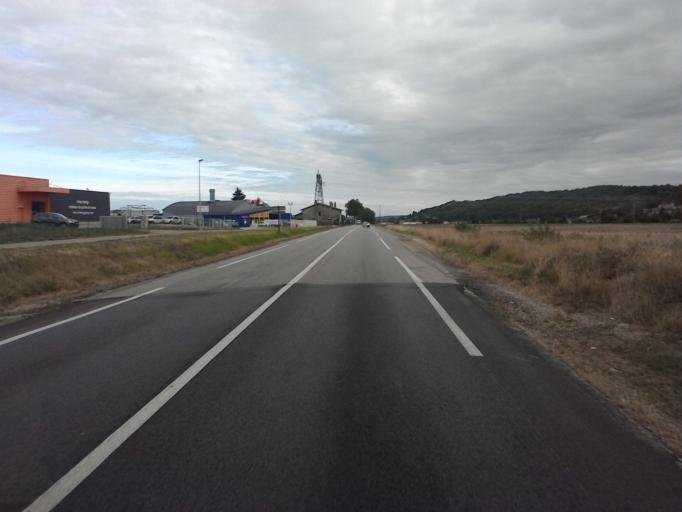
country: FR
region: Rhone-Alpes
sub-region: Departement de l'Ain
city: Vaux-en-Bugey
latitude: 45.9275
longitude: 5.3382
